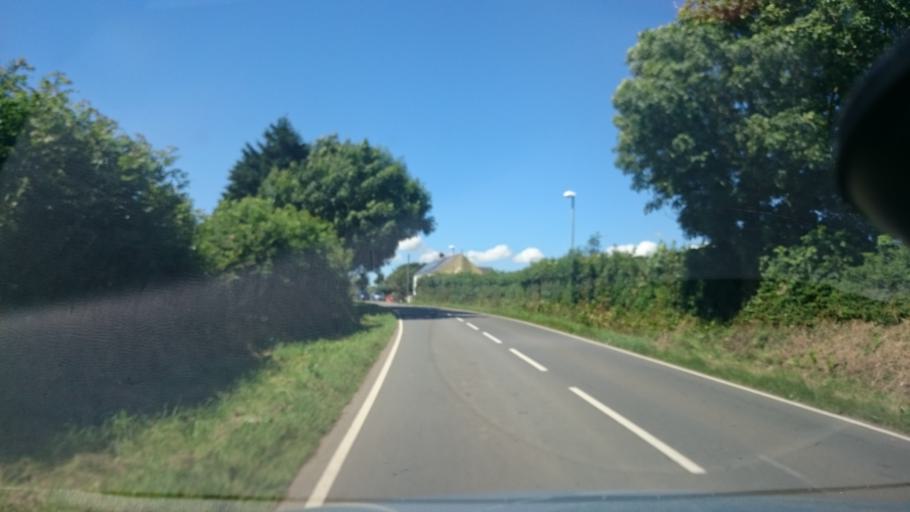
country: GB
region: Wales
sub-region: Pembrokeshire
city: Llangwm
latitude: 51.7359
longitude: -4.9248
